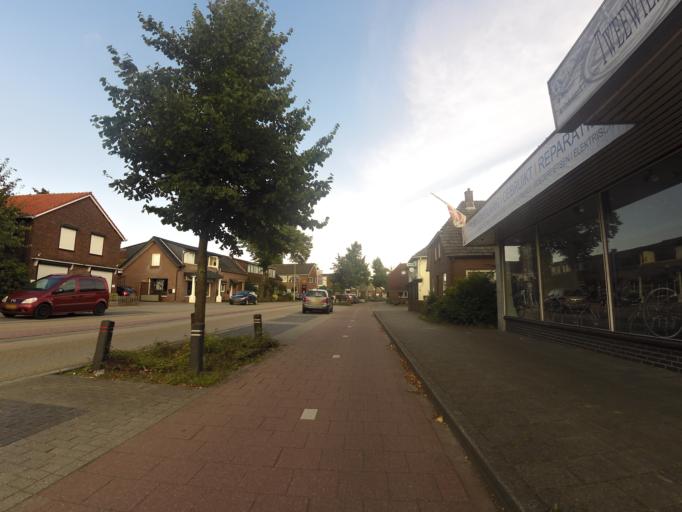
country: NL
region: Gelderland
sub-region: Oude IJsselstreek
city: Gendringen
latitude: 51.9285
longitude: 6.3466
